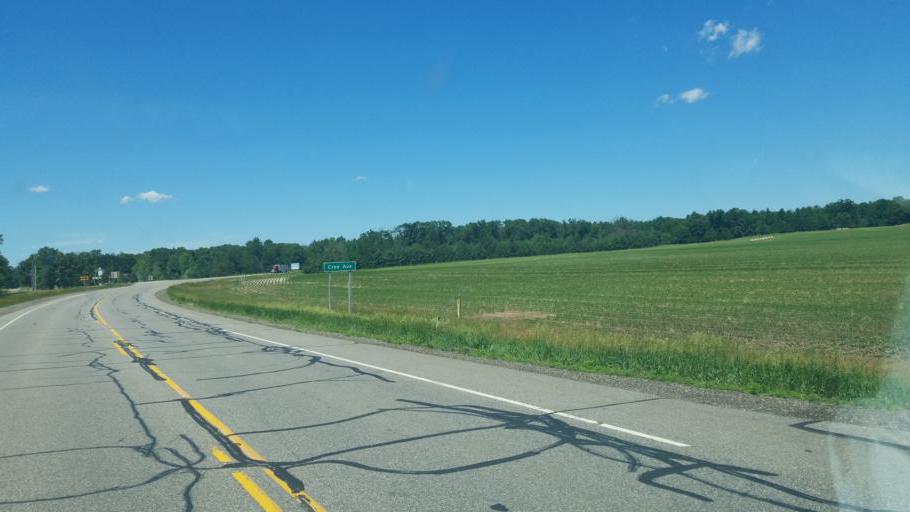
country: US
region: Wisconsin
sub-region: Adams County
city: Friendship
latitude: 44.0396
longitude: -89.9558
